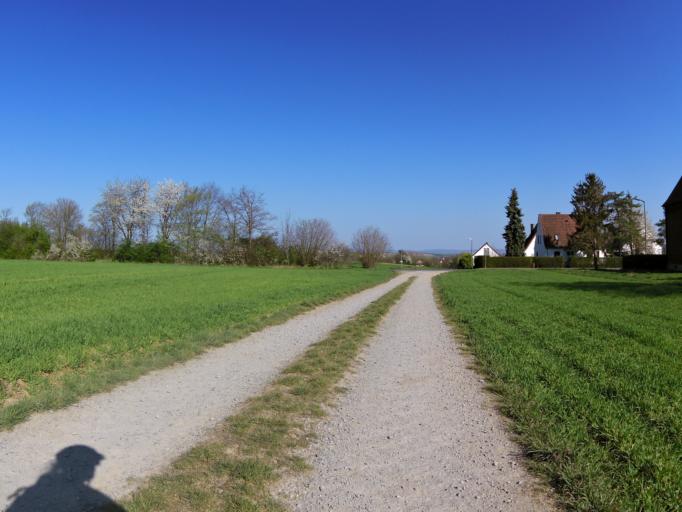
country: DE
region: Bavaria
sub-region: Regierungsbezirk Unterfranken
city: Prosselsheim
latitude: 49.8266
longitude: 10.1056
